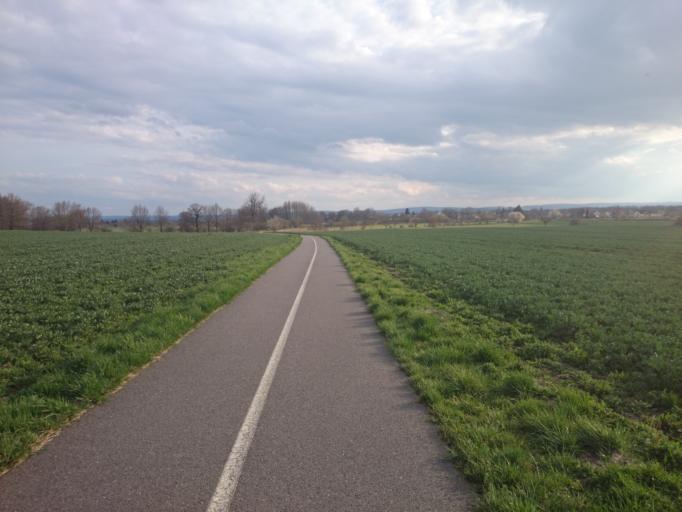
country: CZ
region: Pardubicky
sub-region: Okres Pardubice
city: Pardubice
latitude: 50.0071
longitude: 15.7613
